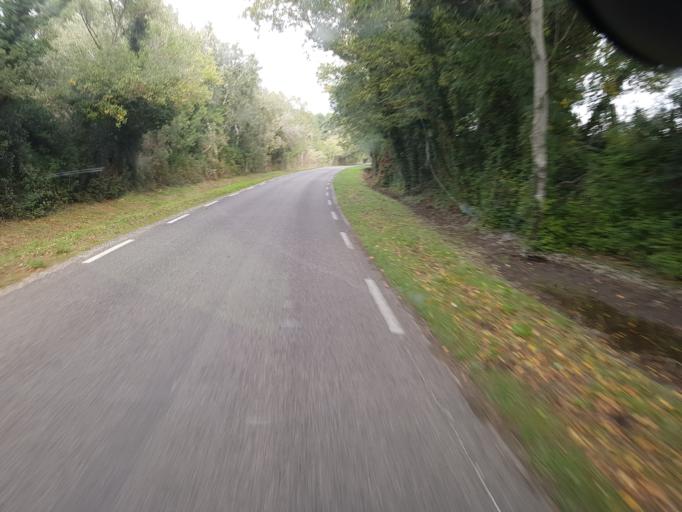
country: FR
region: Languedoc-Roussillon
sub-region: Departement du Gard
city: Aramon
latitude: 43.8721
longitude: 4.6581
